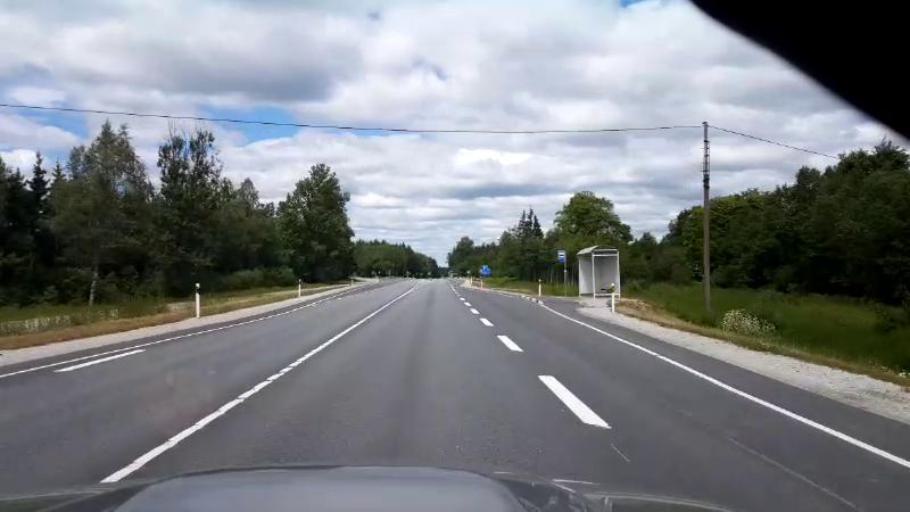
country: EE
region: Raplamaa
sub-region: Maerjamaa vald
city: Marjamaa
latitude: 58.8126
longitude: 24.4125
